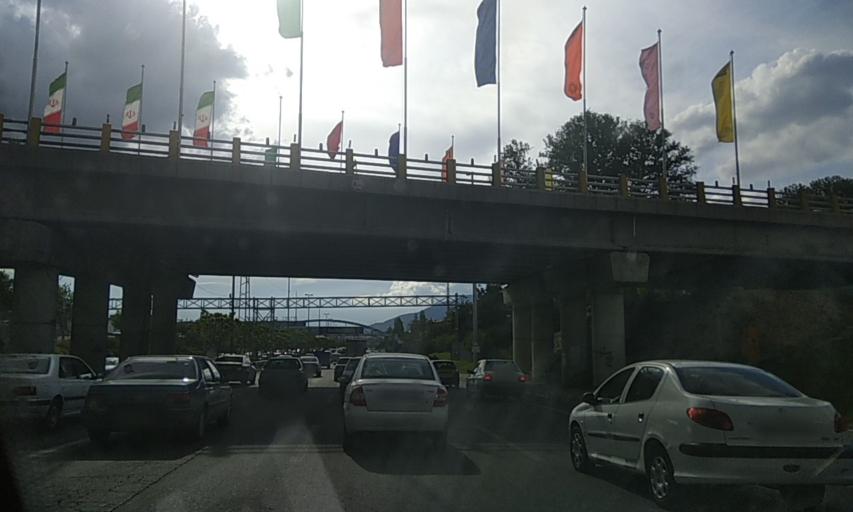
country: IR
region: Tehran
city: Tehran
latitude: 35.7540
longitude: 51.2793
